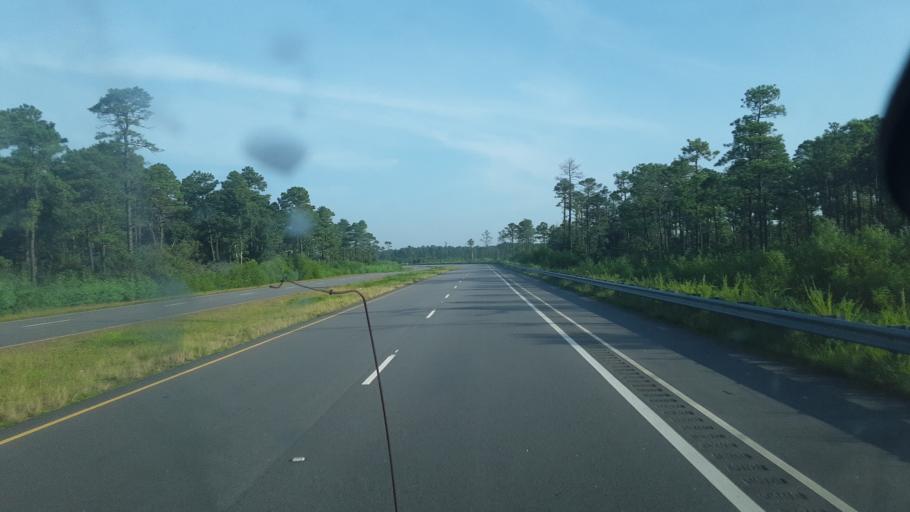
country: US
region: South Carolina
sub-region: Horry County
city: Forestbrook
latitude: 33.7954
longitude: -78.8826
